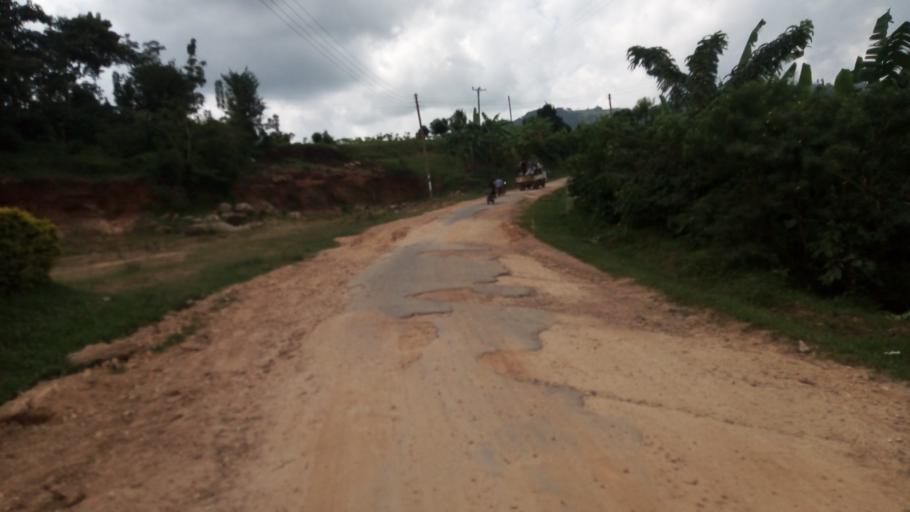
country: UG
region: Eastern Region
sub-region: Mbale District
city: Mbale
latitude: 1.0702
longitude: 34.2129
